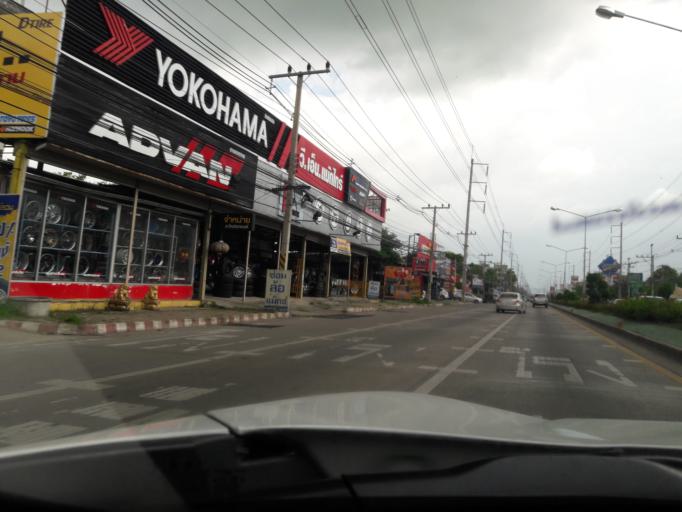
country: TH
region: Lop Buri
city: Lop Buri
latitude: 14.7878
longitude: 100.6778
